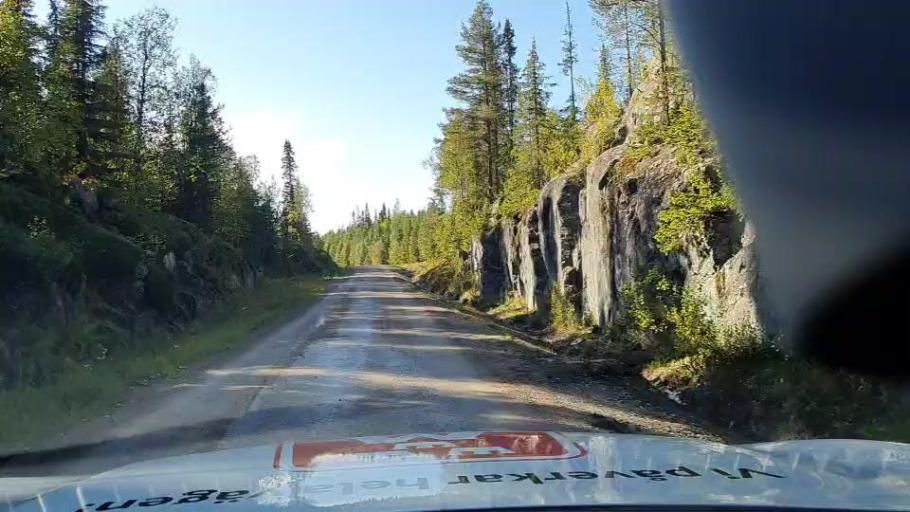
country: SE
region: Jaemtland
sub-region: Stroemsunds Kommun
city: Stroemsund
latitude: 64.5085
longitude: 15.1423
